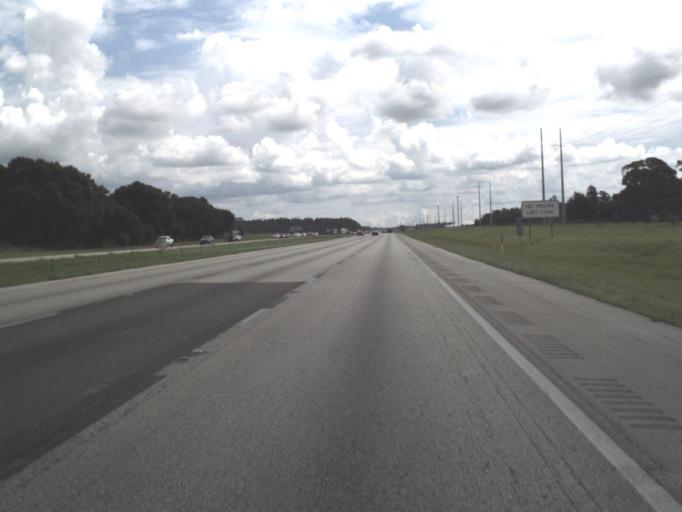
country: US
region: Florida
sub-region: Polk County
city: Polk City
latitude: 28.1444
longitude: -81.8825
